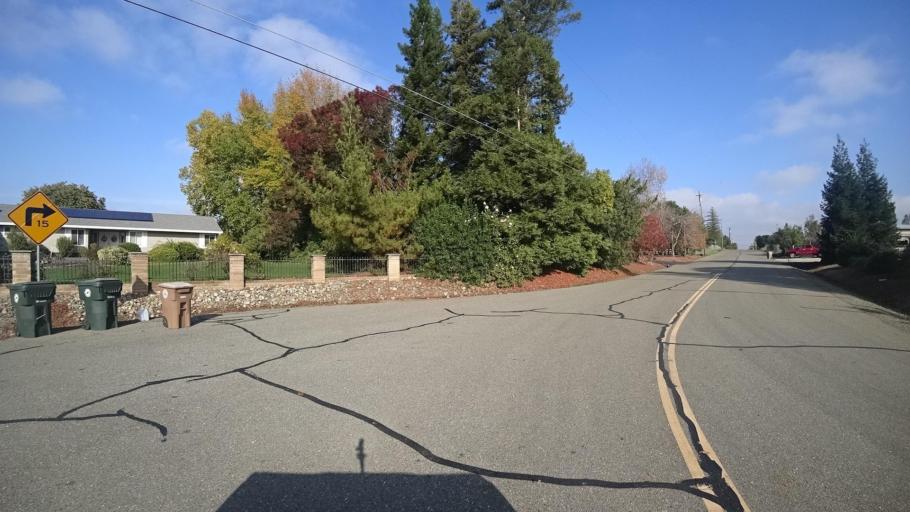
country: US
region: California
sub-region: Sacramento County
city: Vineyard
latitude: 38.4442
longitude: -121.3575
